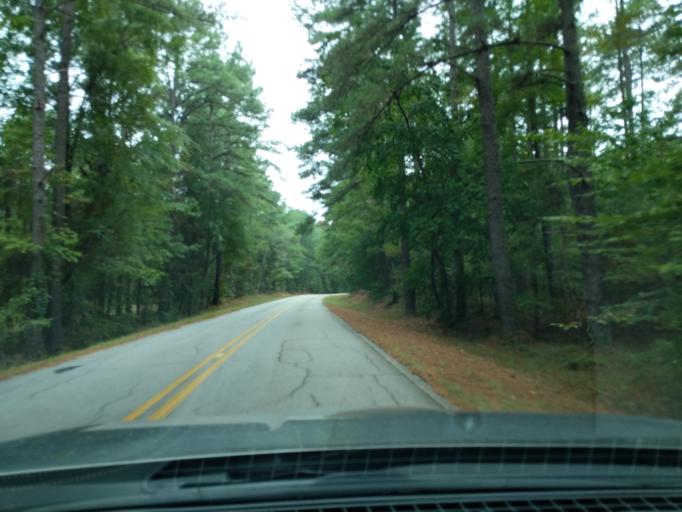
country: US
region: Georgia
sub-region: Columbia County
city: Appling
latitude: 33.6385
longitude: -82.3911
